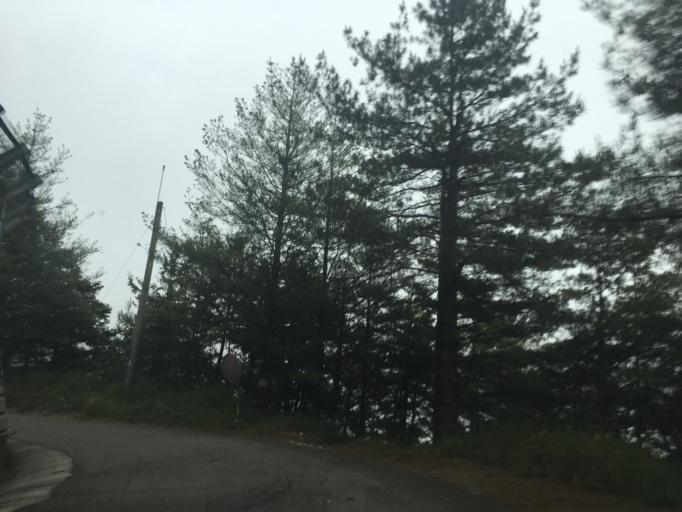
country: TW
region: Taiwan
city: Fengyuan
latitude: 24.2805
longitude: 121.0281
